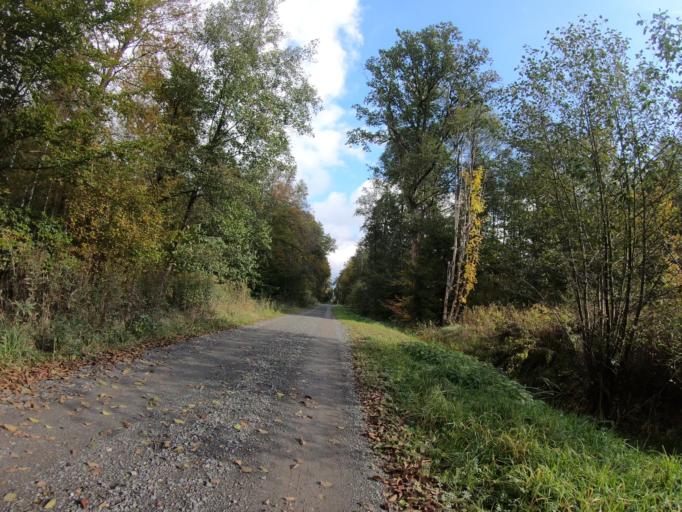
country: DE
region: Lower Saxony
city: Wahrenholz
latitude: 52.5948
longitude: 10.6299
